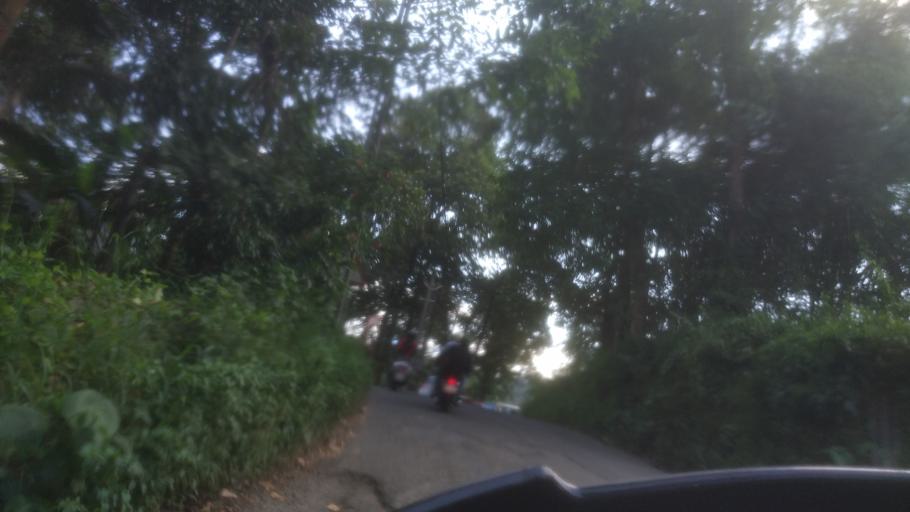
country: IN
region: Kerala
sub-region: Ernakulam
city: Muvattupula
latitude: 9.9963
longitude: 76.6125
